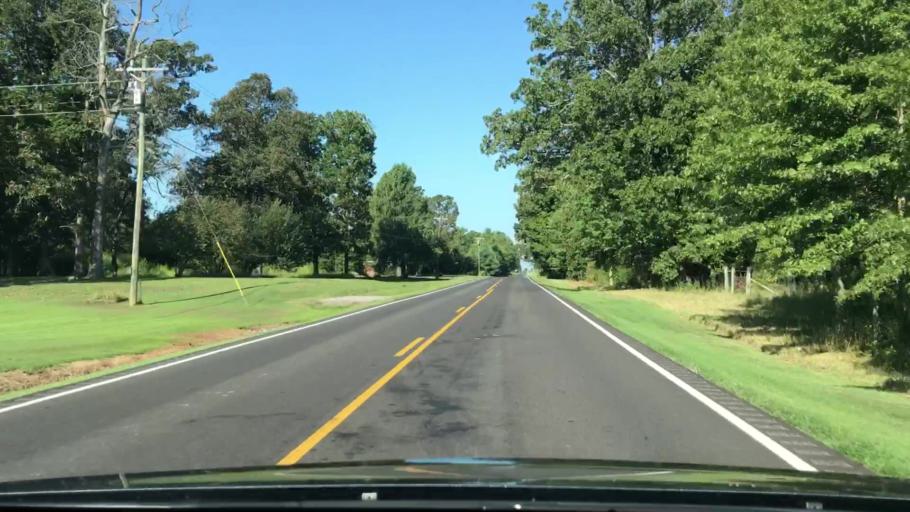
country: US
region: Kentucky
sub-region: Marshall County
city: Benton
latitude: 36.7647
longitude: -88.3388
